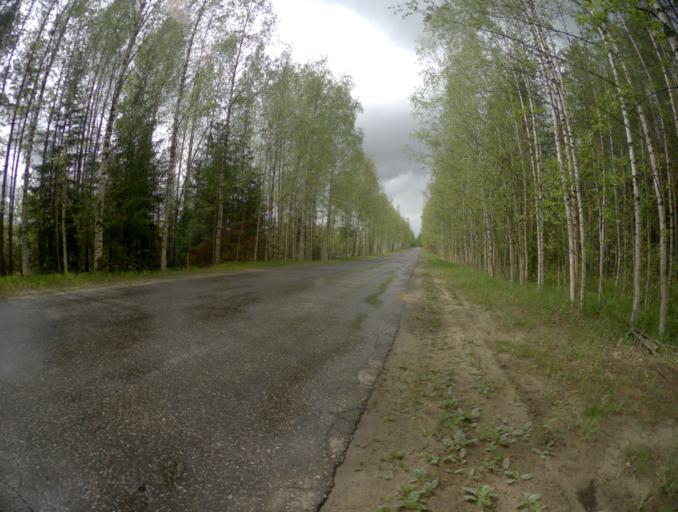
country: RU
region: Vladimir
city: Zolotkovo
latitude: 55.3533
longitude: 40.9136
